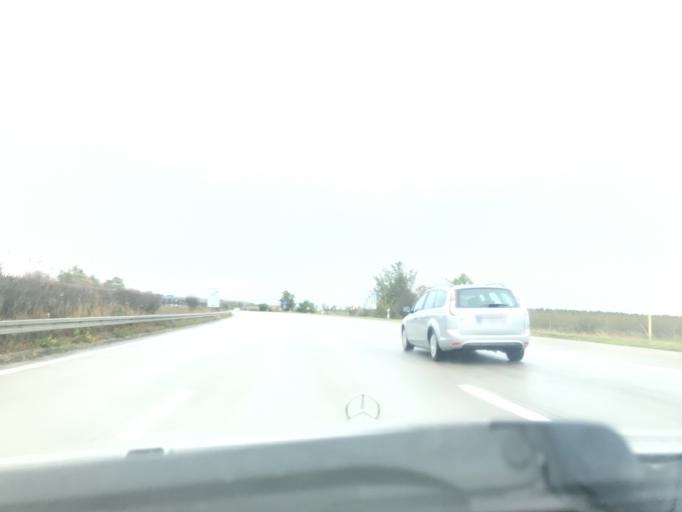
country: DE
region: Brandenburg
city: Woltersdorf
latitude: 52.4825
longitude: 13.7545
